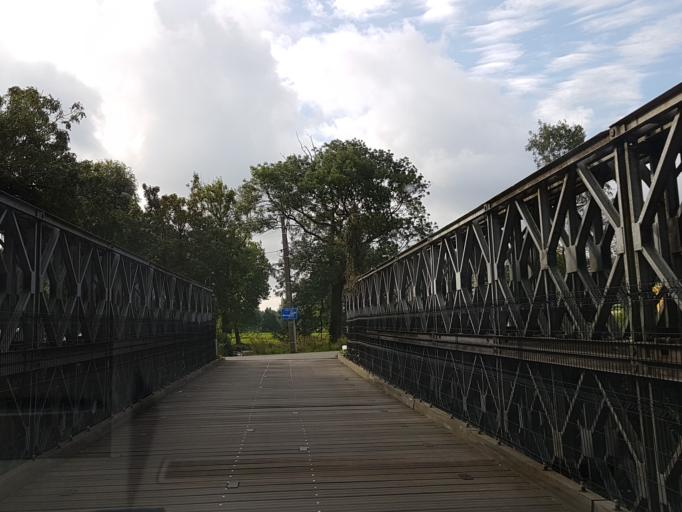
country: BE
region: Flanders
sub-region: Provincie Oost-Vlaanderen
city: Sint-Martens-Latem
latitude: 51.0499
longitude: 3.6652
